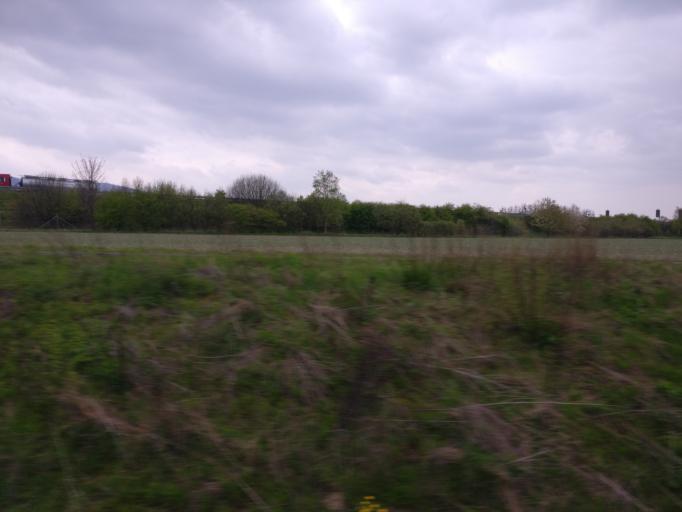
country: DE
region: Saxony-Anhalt
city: Stapelburg
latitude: 51.9096
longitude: 10.6748
